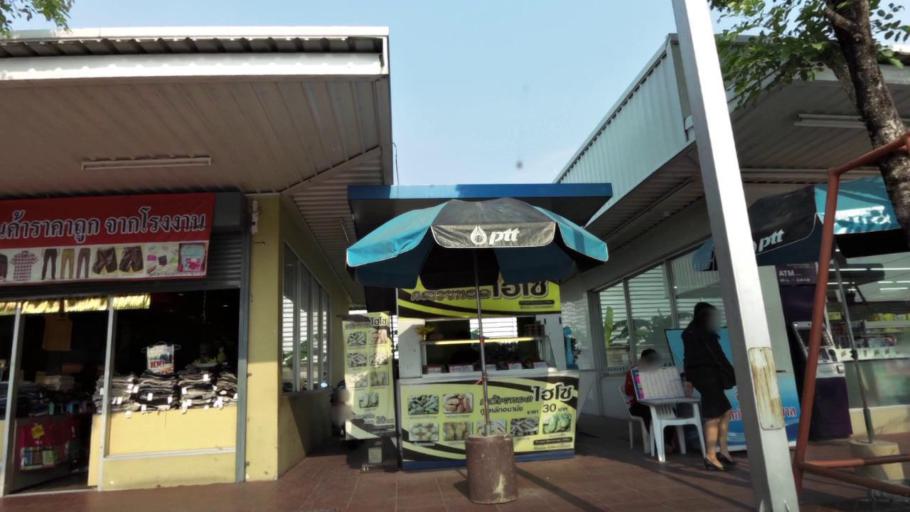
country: TH
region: Phra Nakhon Si Ayutthaya
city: Phra Nakhon Si Ayutthaya
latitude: 14.3276
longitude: 100.6241
